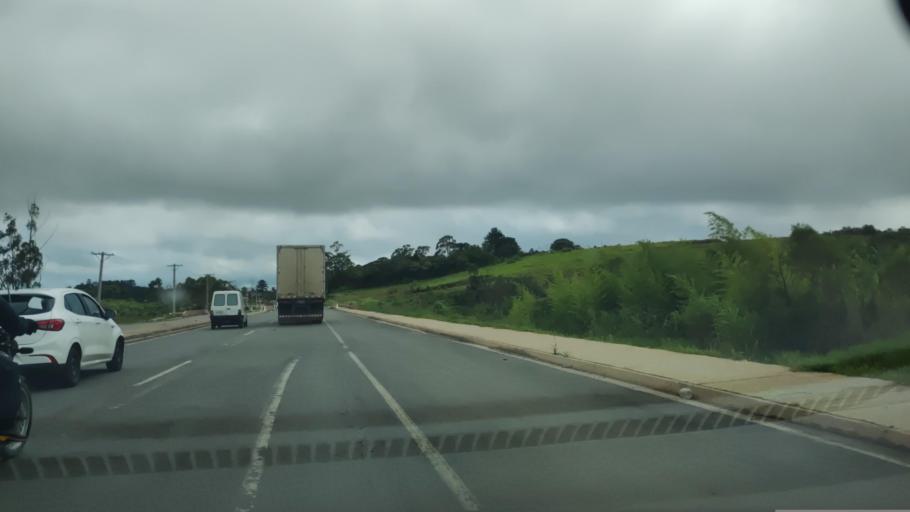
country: BR
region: Sao Paulo
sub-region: Vargem Grande Paulista
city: Vargem Grande Paulista
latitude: -23.6303
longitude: -47.0550
